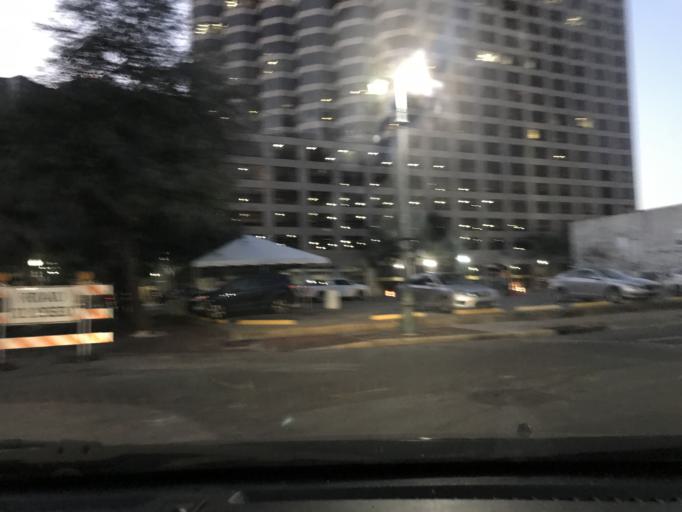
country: US
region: Louisiana
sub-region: Orleans Parish
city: New Orleans
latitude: 29.9492
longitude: -90.0745
